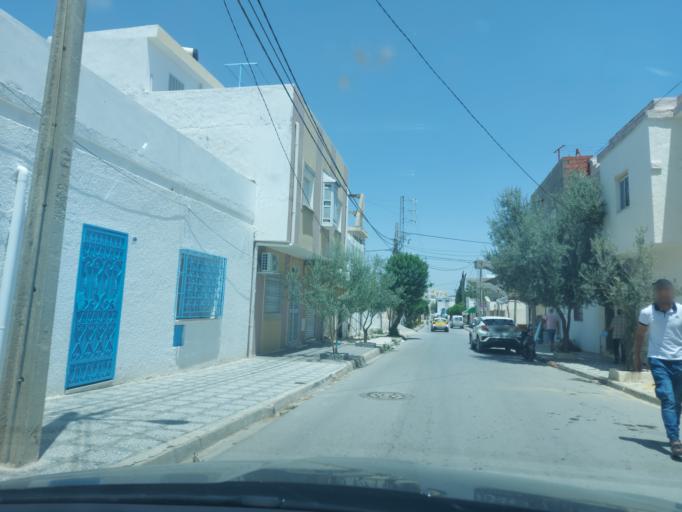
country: TN
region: Silyanah
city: Siliana
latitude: 36.0891
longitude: 9.3703
